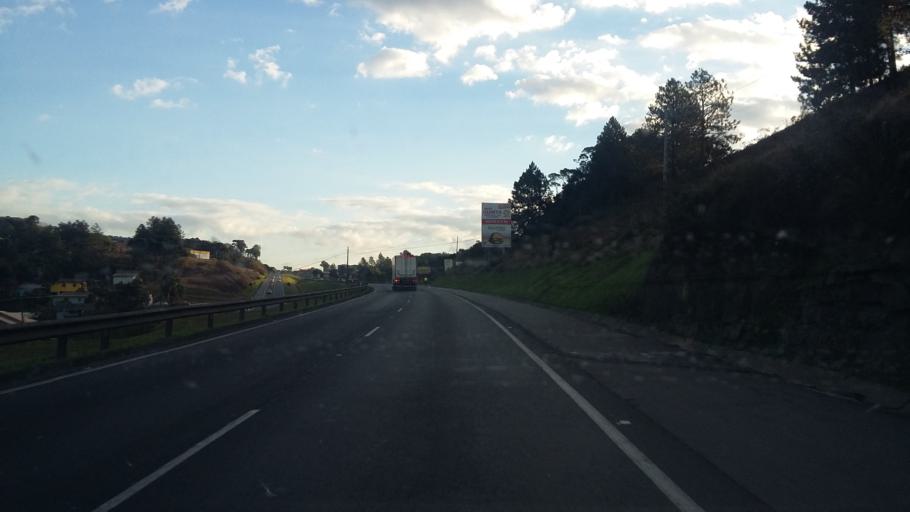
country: BR
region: Parana
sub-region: Curitiba
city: Curitiba
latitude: -25.4284
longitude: -49.3921
